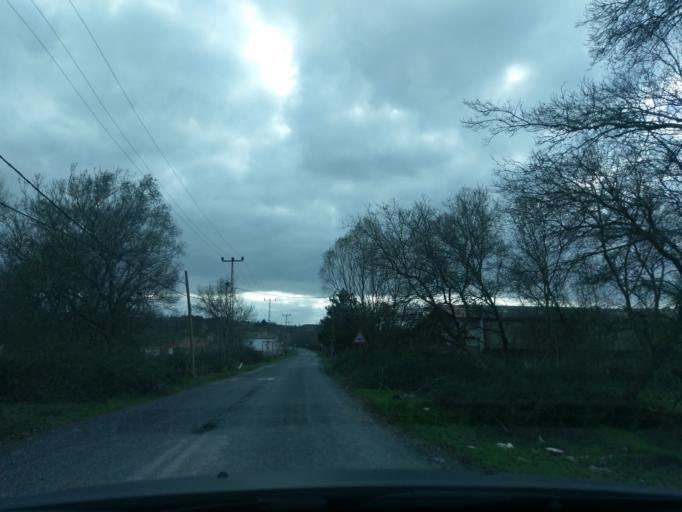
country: TR
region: Istanbul
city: Durusu
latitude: 41.2964
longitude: 28.6771
